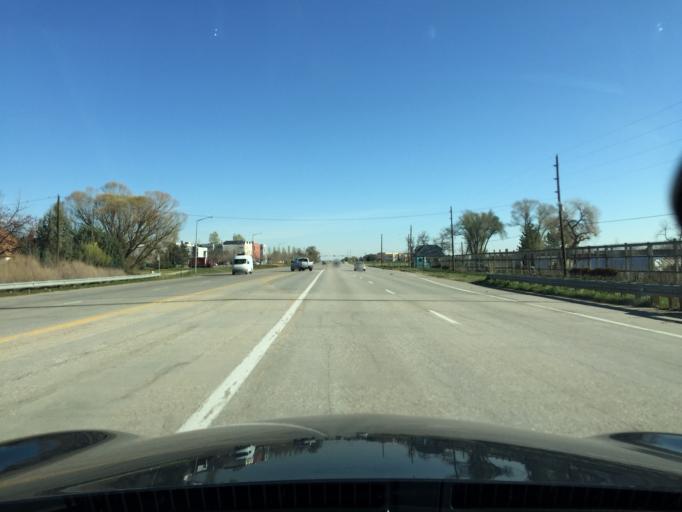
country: US
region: Colorado
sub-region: Boulder County
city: Longmont
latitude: 40.1322
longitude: -105.1025
